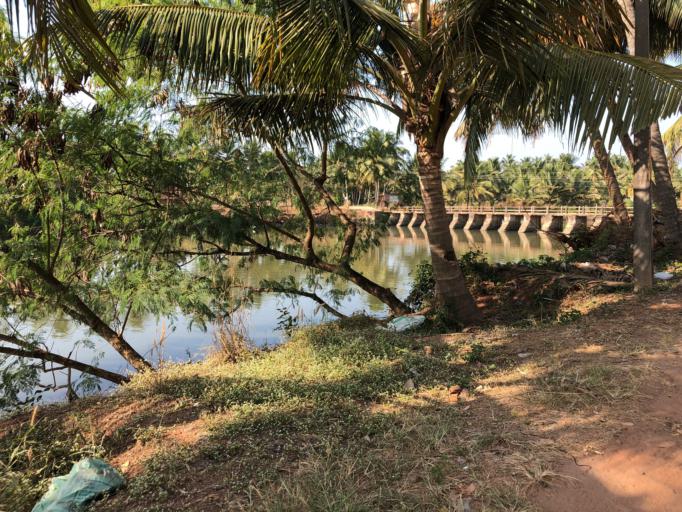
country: IN
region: Karnataka
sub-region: Dakshina Kannada
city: Mangalore
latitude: 12.9044
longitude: 74.8215
